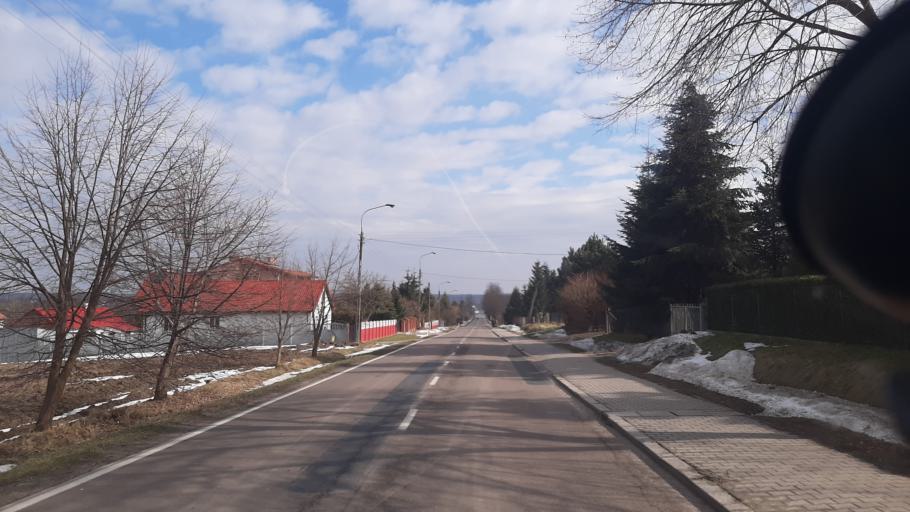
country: PL
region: Lublin Voivodeship
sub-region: Powiat lubelski
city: Niemce
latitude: 51.3587
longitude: 22.6107
